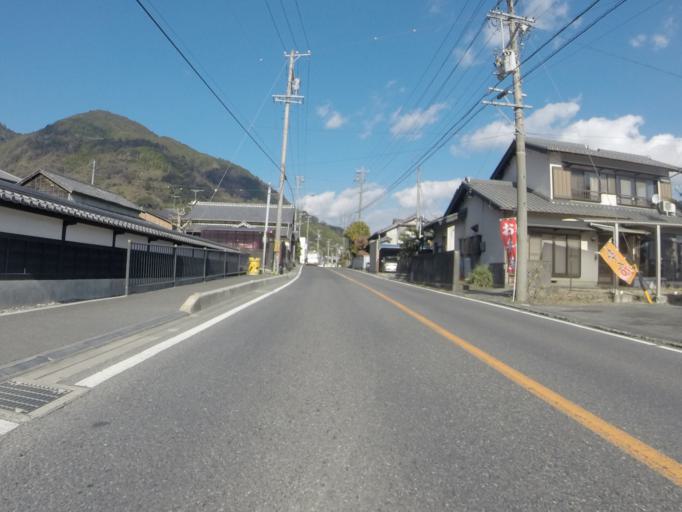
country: JP
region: Shizuoka
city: Shizuoka-shi
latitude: 35.0824
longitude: 138.5145
